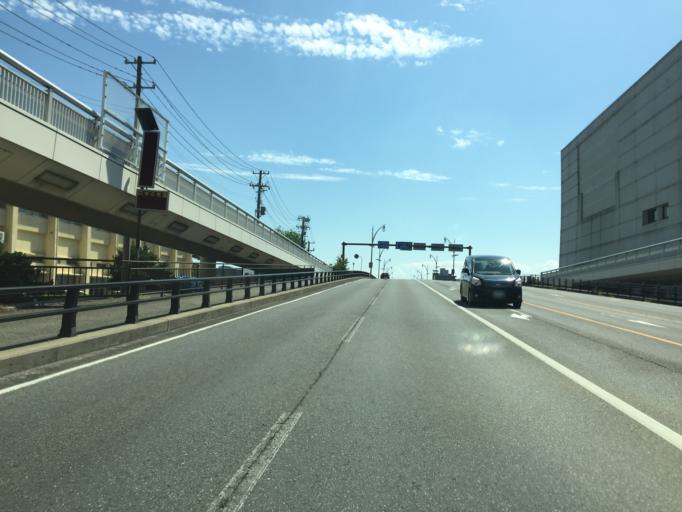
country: JP
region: Niigata
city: Niigata-shi
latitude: 37.9141
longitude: 139.0419
